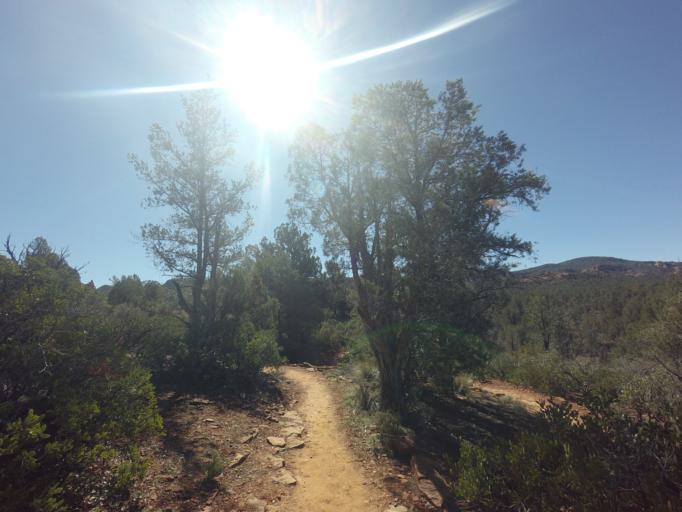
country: US
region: Arizona
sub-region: Yavapai County
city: West Sedona
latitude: 34.8067
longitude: -111.8226
